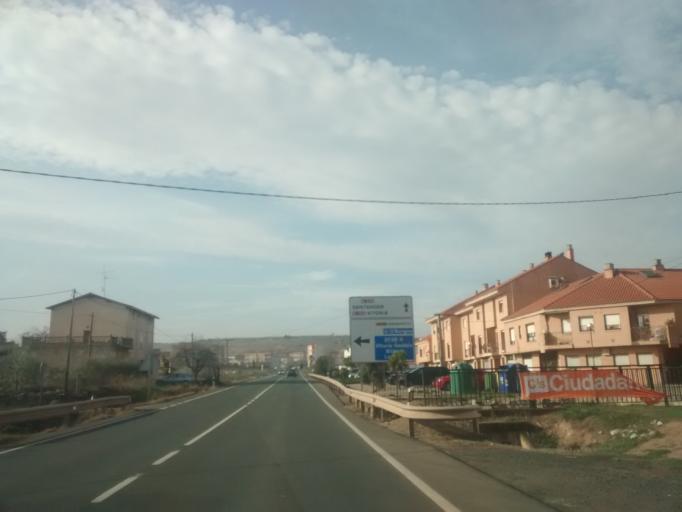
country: ES
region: La Rioja
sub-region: Provincia de La Rioja
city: Fuenmayor
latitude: 42.4636
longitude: -2.5614
